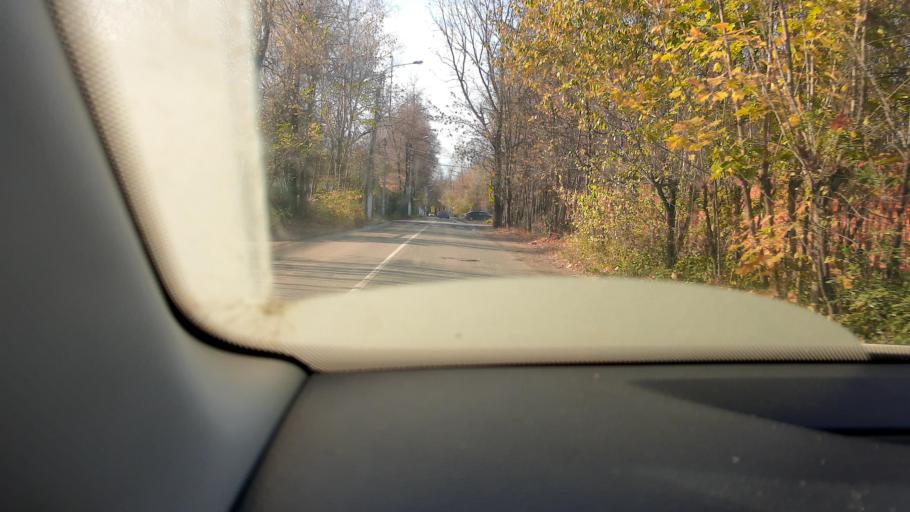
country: RU
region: Moskovskaya
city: Shcherbinka
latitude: 55.5308
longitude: 37.6010
